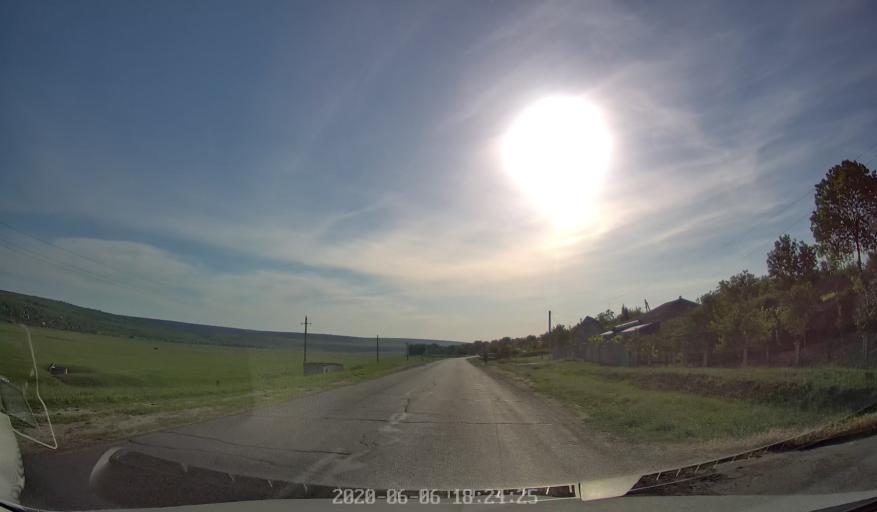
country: MD
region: Chisinau
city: Vadul lui Voda
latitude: 47.1163
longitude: 29.0521
